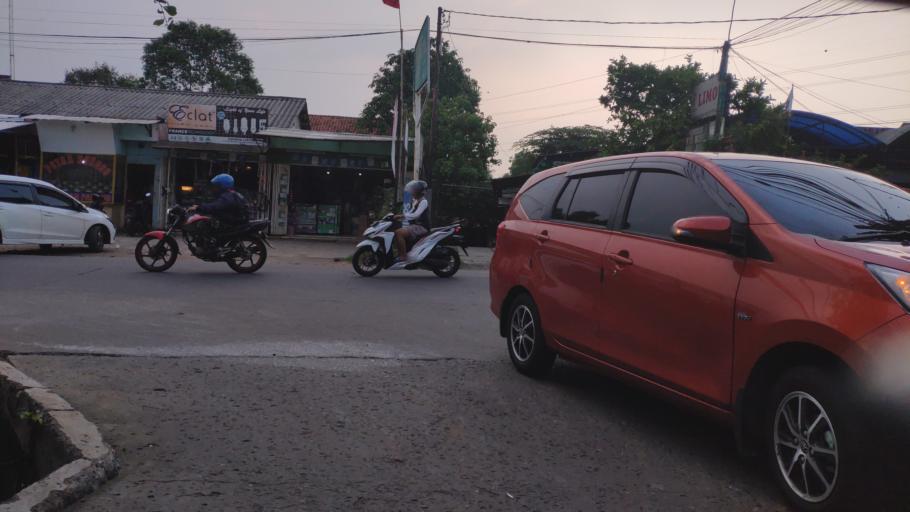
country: ID
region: West Java
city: Pamulang
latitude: -6.3605
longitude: 106.7759
